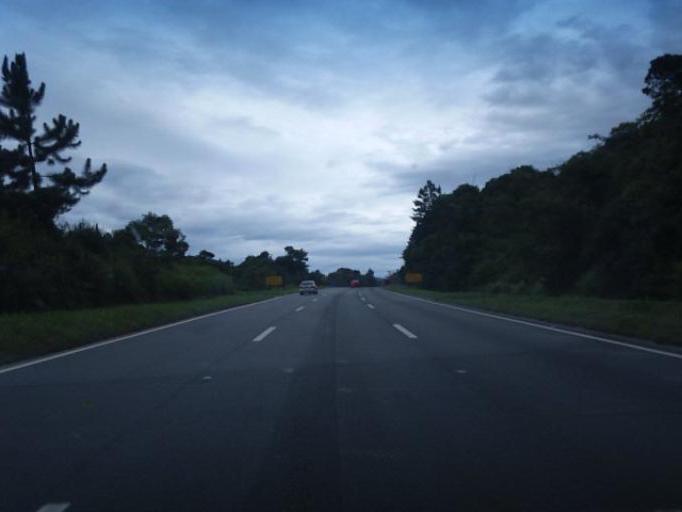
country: BR
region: Sao Paulo
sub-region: Cajati
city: Cajati
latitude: -24.9795
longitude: -48.5060
